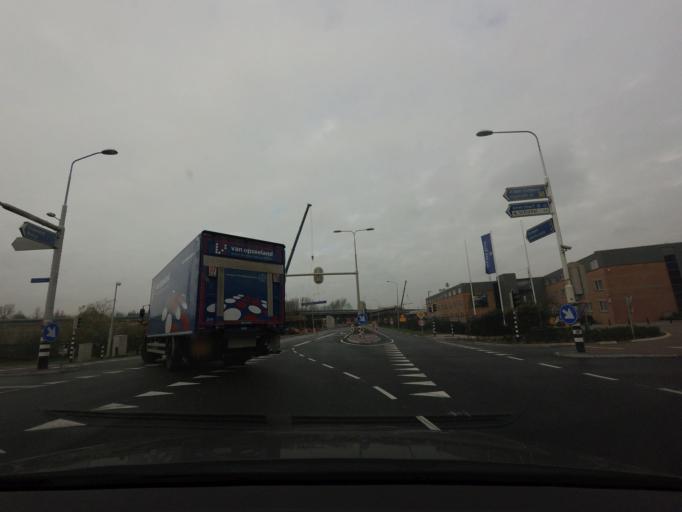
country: NL
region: North Holland
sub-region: Gemeente Amsterdam
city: Driemond
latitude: 52.3153
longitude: 4.9955
